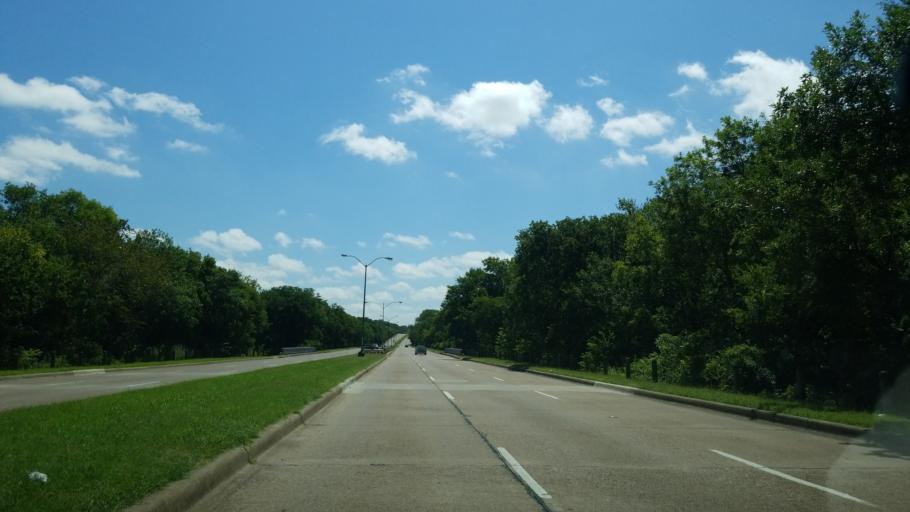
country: US
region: Texas
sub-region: Dallas County
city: Balch Springs
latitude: 32.7492
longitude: -96.7135
